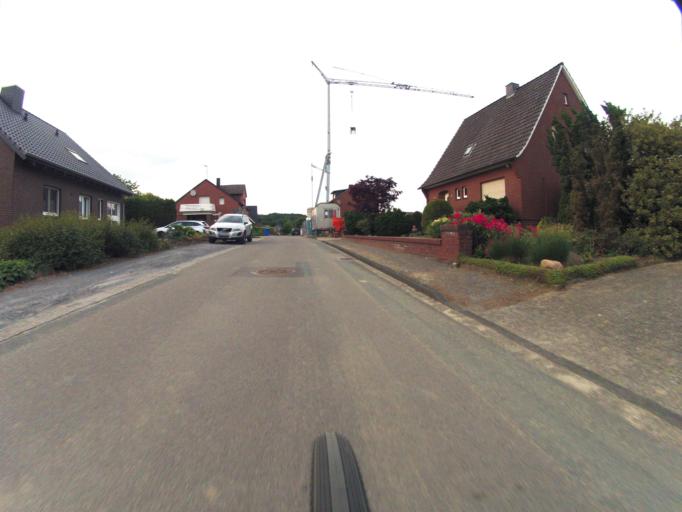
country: DE
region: North Rhine-Westphalia
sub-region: Regierungsbezirk Munster
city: Mettingen
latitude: 52.2683
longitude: 7.7726
